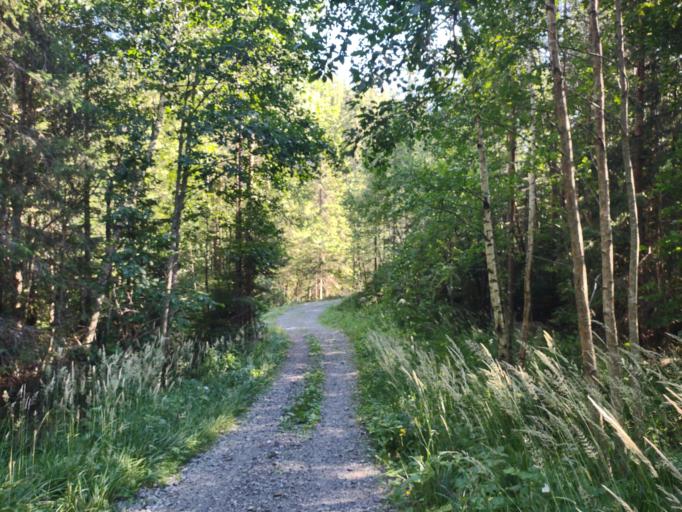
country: NO
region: Akershus
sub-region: Raelingen
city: Fjerdingby
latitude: 59.8848
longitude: 11.0420
